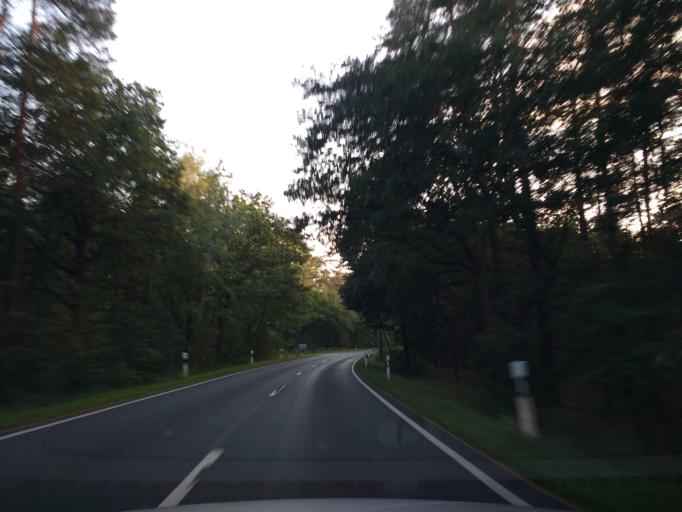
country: DE
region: Lower Saxony
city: Neustadt am Rubenberge
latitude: 52.5376
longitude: 9.3858
